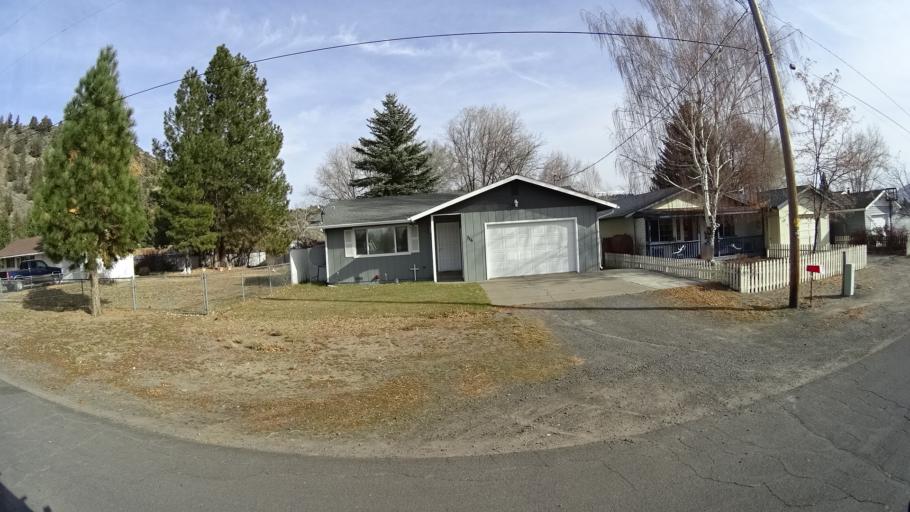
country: US
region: Oregon
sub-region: Klamath County
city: Klamath Falls
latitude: 41.9709
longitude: -121.9145
